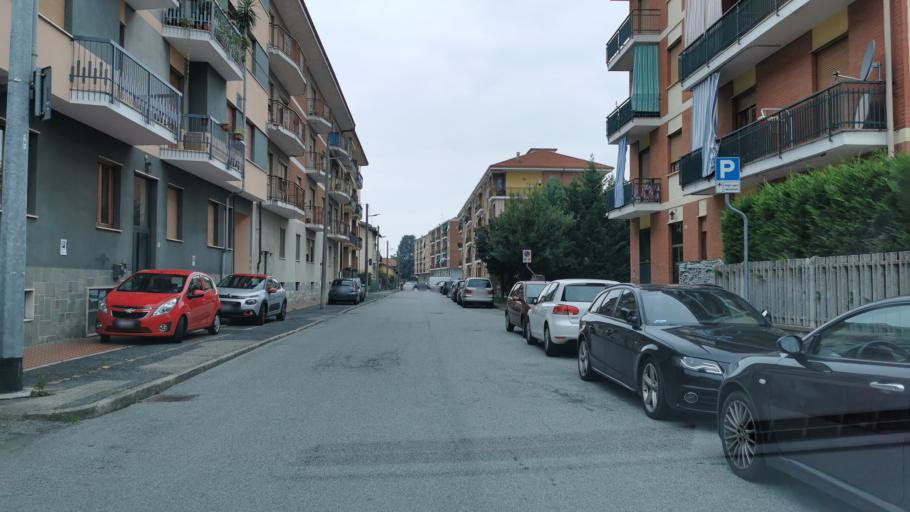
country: IT
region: Piedmont
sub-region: Provincia di Cuneo
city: Bra
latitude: 44.6924
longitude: 7.8585
